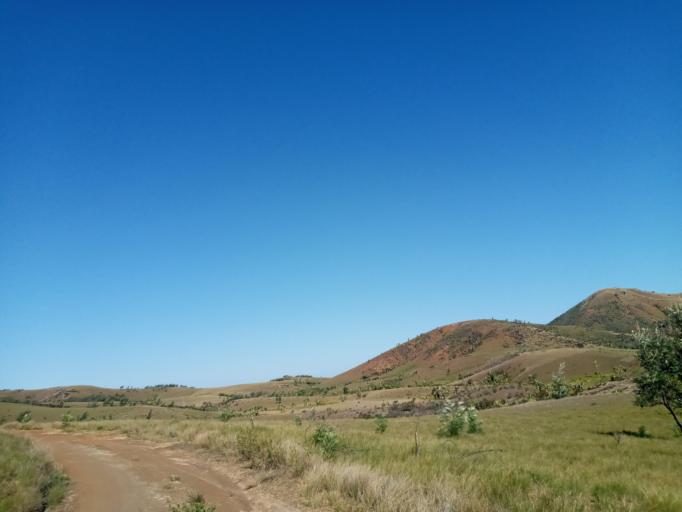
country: MG
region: Anosy
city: Fort Dauphin
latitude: -24.9114
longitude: 47.0703
